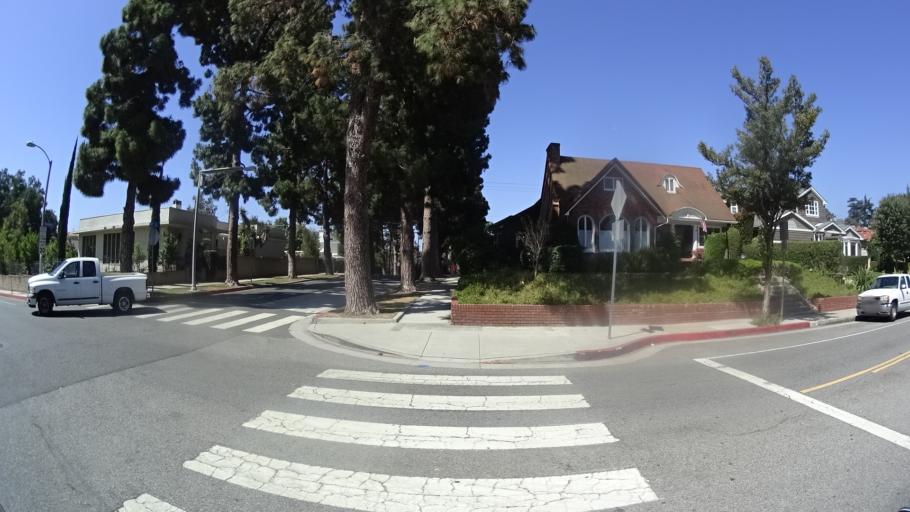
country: US
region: California
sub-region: Los Angeles County
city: Santa Monica
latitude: 34.0459
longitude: -118.4890
